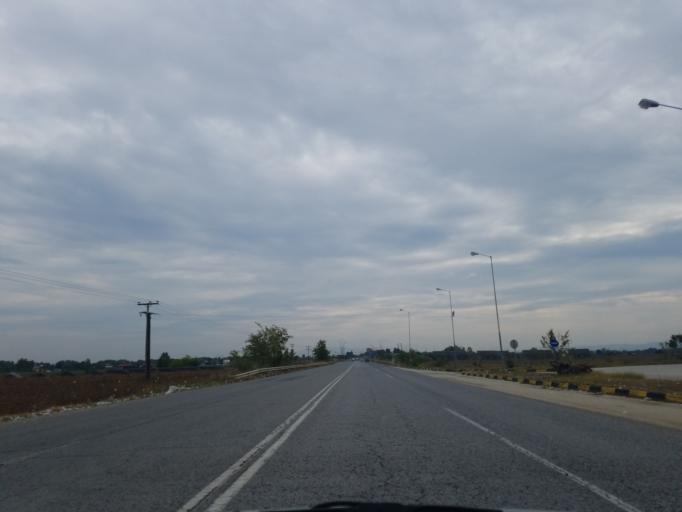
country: GR
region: Thessaly
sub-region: Nomos Kardhitsas
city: Sofades
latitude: 39.3465
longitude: 22.0739
